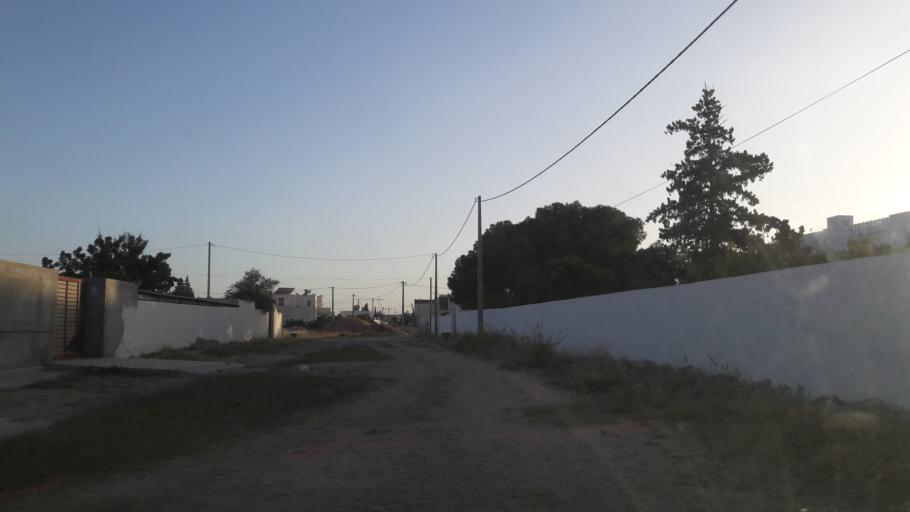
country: TN
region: Safaqis
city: Al Qarmadah
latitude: 34.8197
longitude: 10.7503
